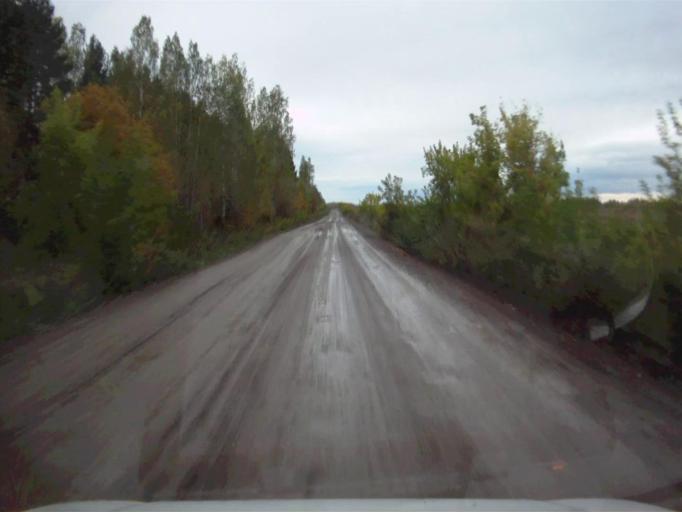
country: RU
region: Sverdlovsk
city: Mikhaylovsk
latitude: 56.1586
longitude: 59.2532
